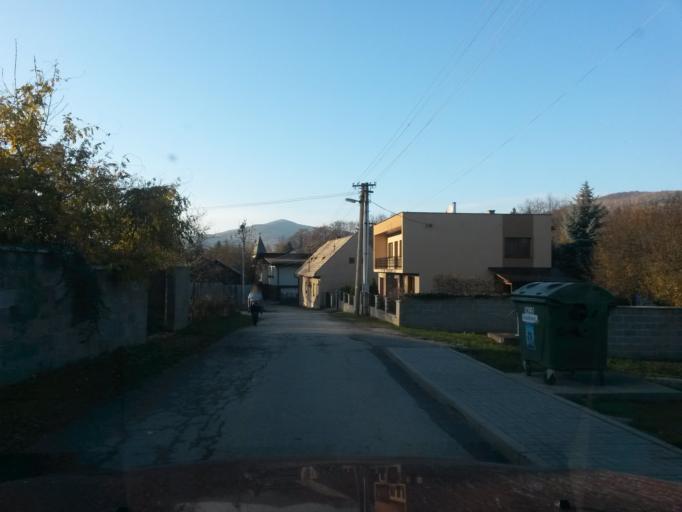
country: SK
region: Kosicky
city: Roznava
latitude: 48.7031
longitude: 20.5119
